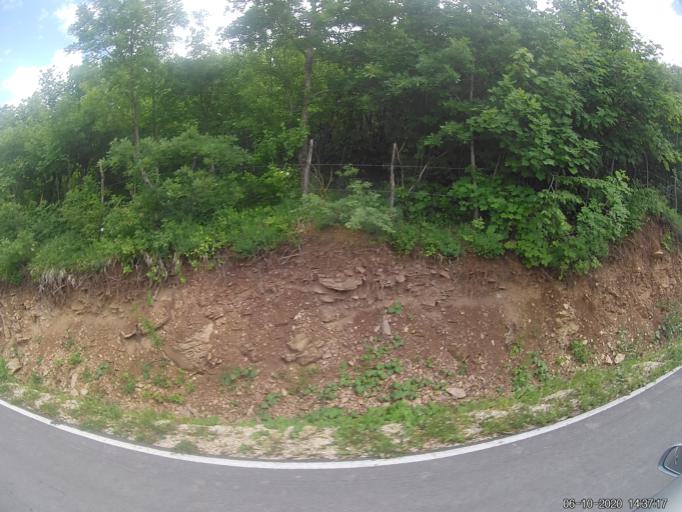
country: XK
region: Prizren
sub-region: Komuna e Therandes
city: Budakovo
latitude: 42.4091
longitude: 20.9398
